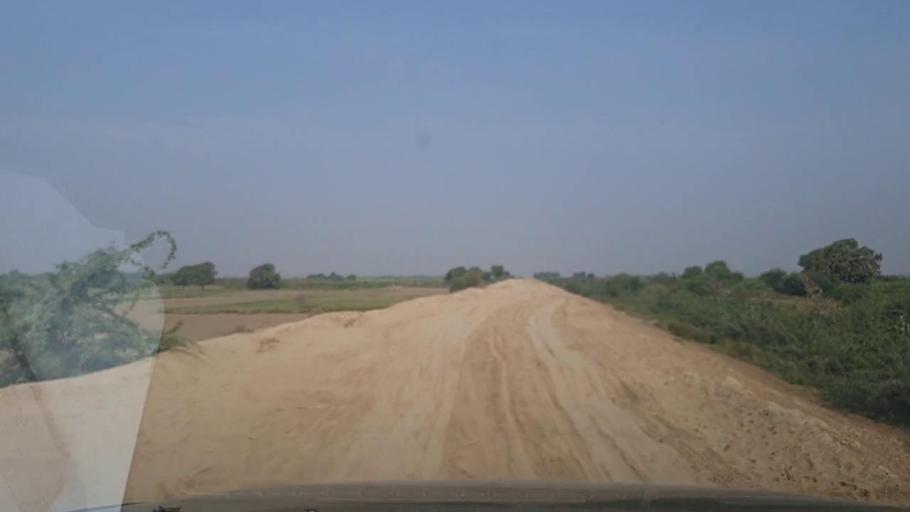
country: PK
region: Sindh
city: Bulri
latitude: 24.9894
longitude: 68.2931
